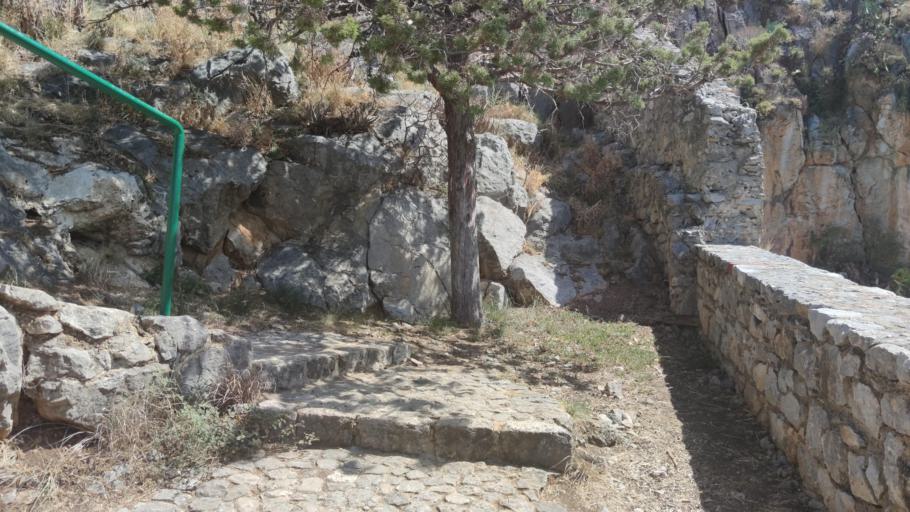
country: IT
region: Sicily
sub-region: Palermo
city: Cefalu
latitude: 38.0367
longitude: 14.0243
